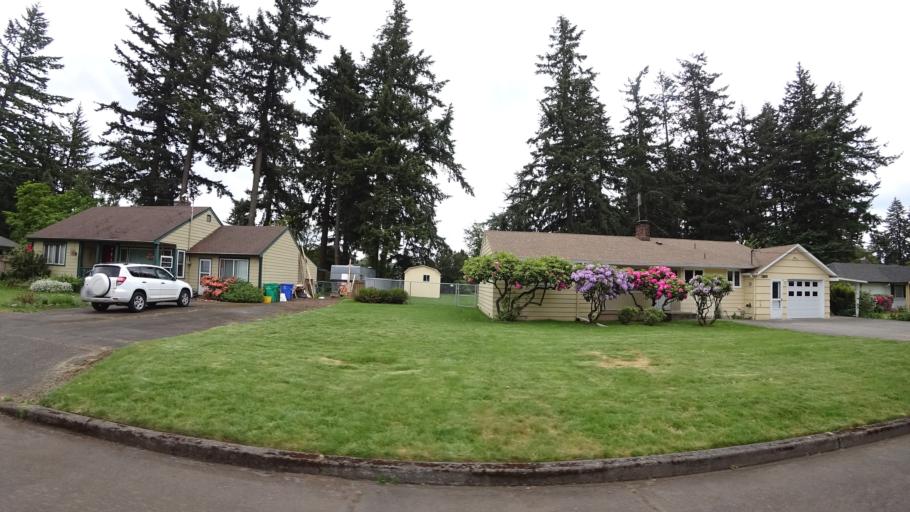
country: US
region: Oregon
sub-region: Multnomah County
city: Lents
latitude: 45.5064
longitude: -122.5447
